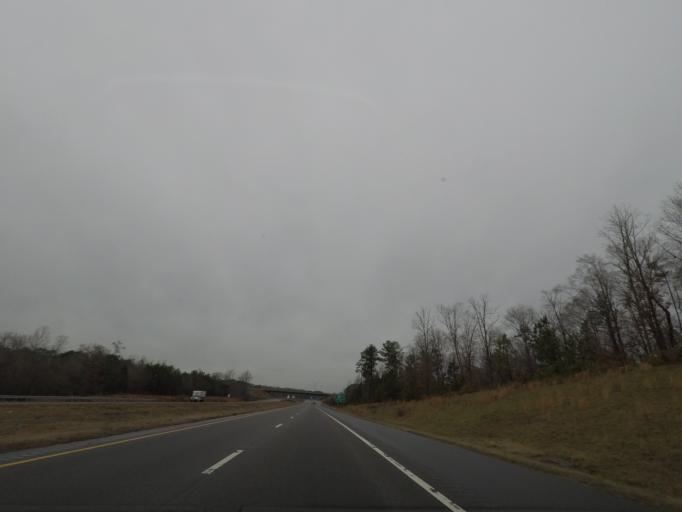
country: US
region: North Carolina
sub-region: Chatham County
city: Farmville
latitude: 35.5394
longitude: -79.2358
